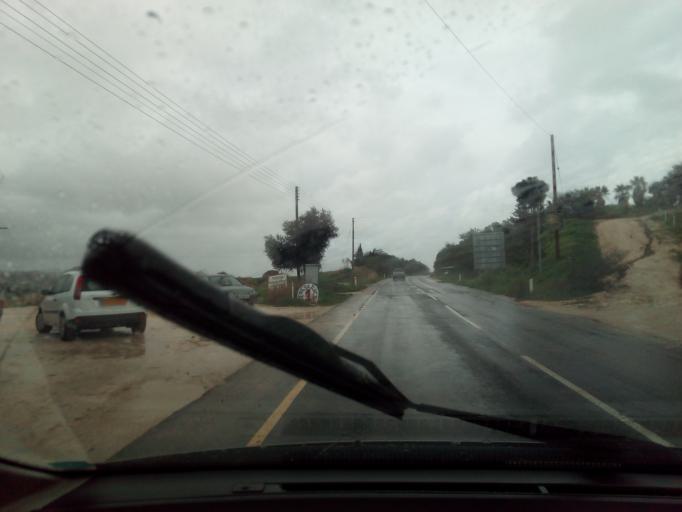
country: CY
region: Pafos
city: Polis
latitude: 34.9967
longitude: 32.4466
